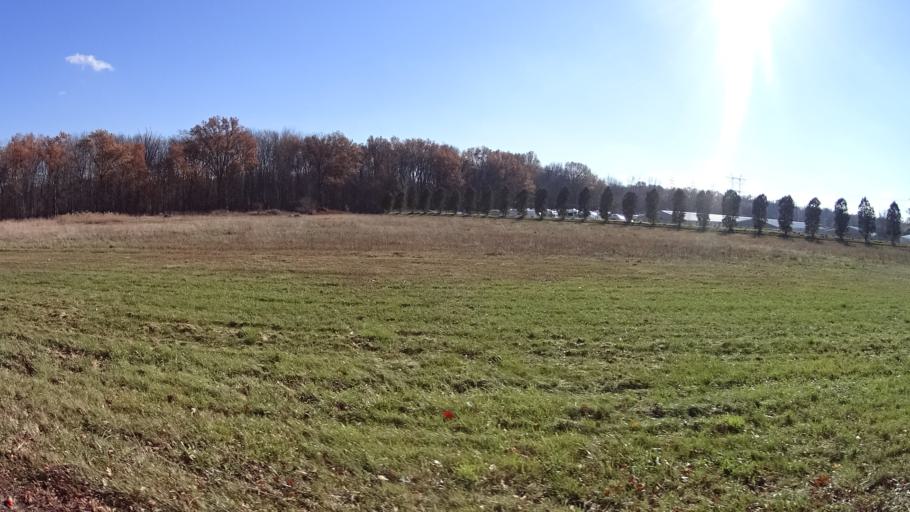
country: US
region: Ohio
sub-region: Lorain County
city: North Ridgeville
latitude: 41.4036
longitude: -81.9856
